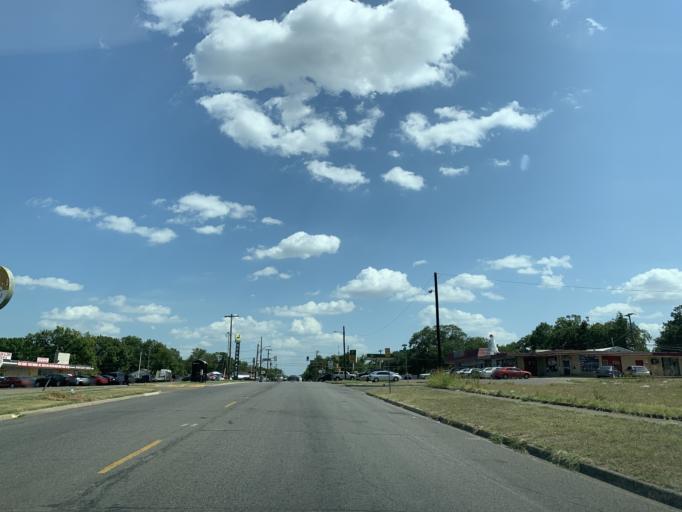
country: US
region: Texas
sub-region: Dallas County
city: Dallas
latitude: 32.7129
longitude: -96.7850
